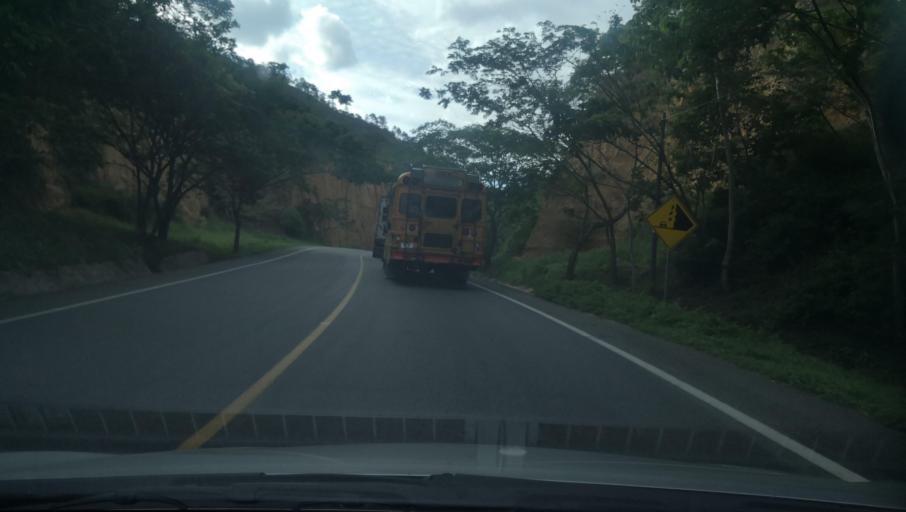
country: NI
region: Nueva Segovia
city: Mozonte
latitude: 13.6882
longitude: -86.4874
